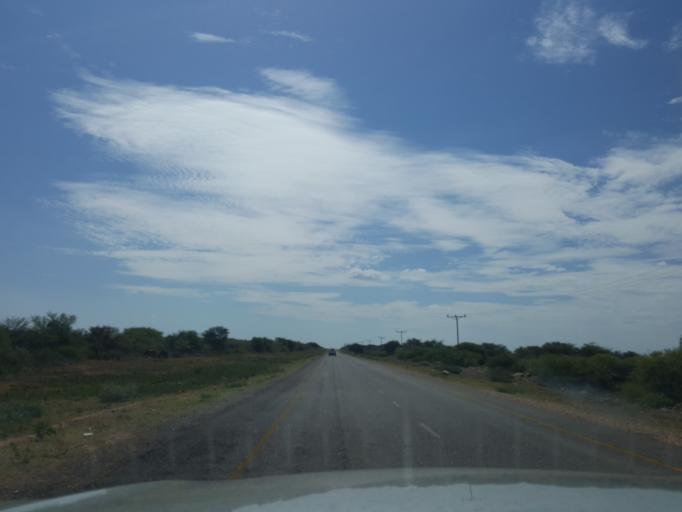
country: BW
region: Kweneng
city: Letlhakeng
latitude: -24.1517
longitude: 25.1571
